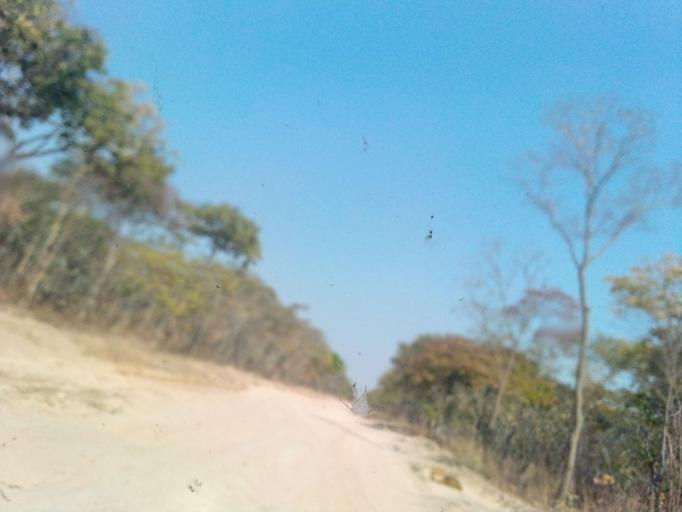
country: ZM
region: Northern
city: Mpika
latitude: -12.2289
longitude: 30.9145
